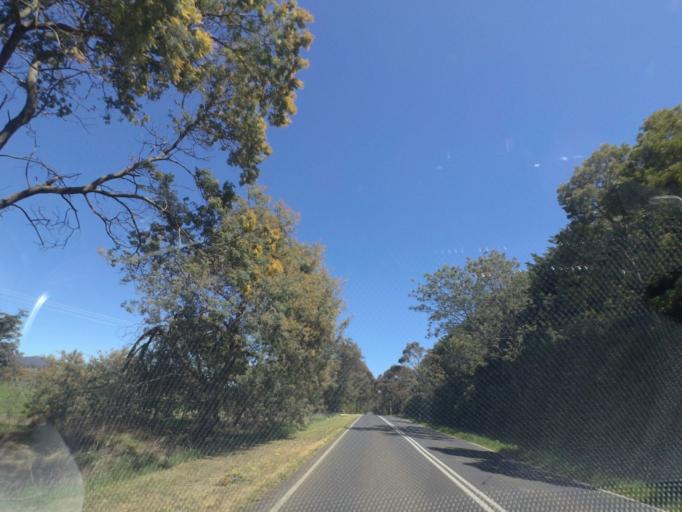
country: AU
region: Victoria
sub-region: Hume
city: Sunbury
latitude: -37.3140
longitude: 144.6636
